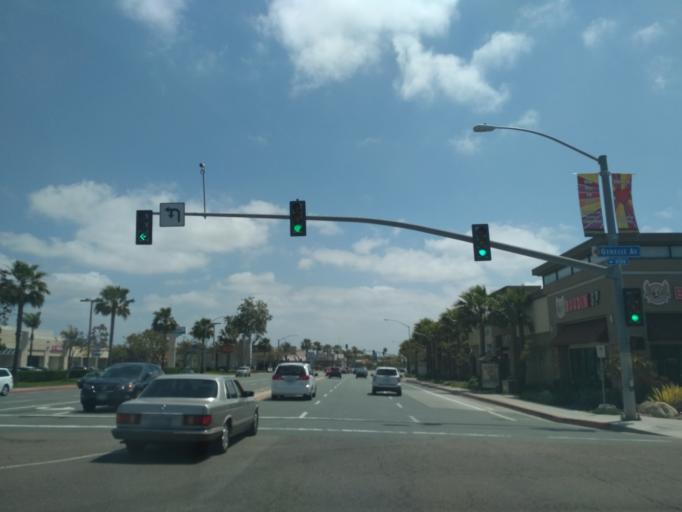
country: US
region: California
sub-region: San Diego County
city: La Jolla
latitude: 32.8193
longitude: -117.1819
